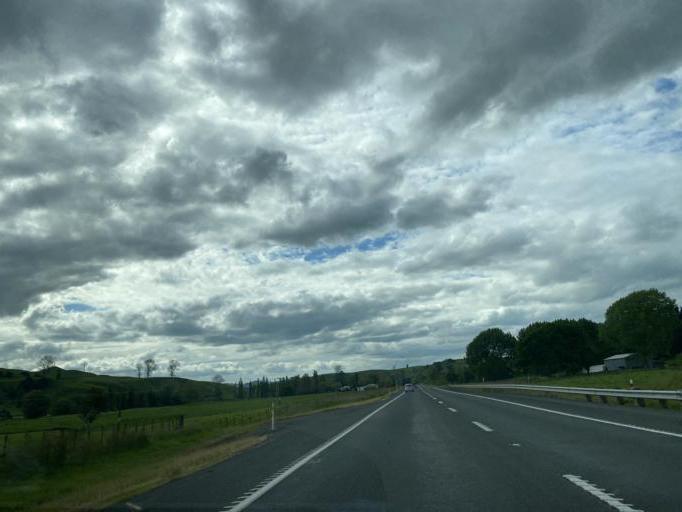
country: NZ
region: Waikato
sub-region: Matamata-Piako District
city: Matamata
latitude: -37.9673
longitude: 175.6897
